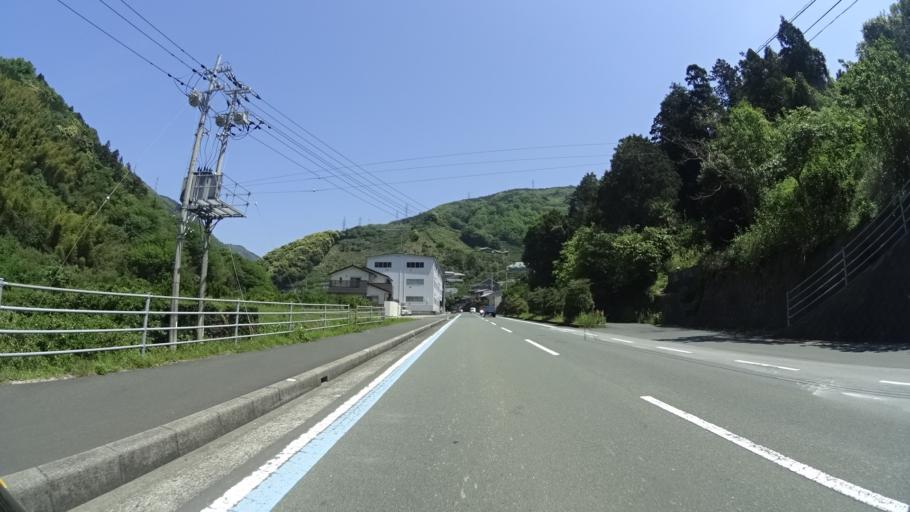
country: JP
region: Ehime
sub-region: Nishiuwa-gun
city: Ikata-cho
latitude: 33.5037
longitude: 132.3970
